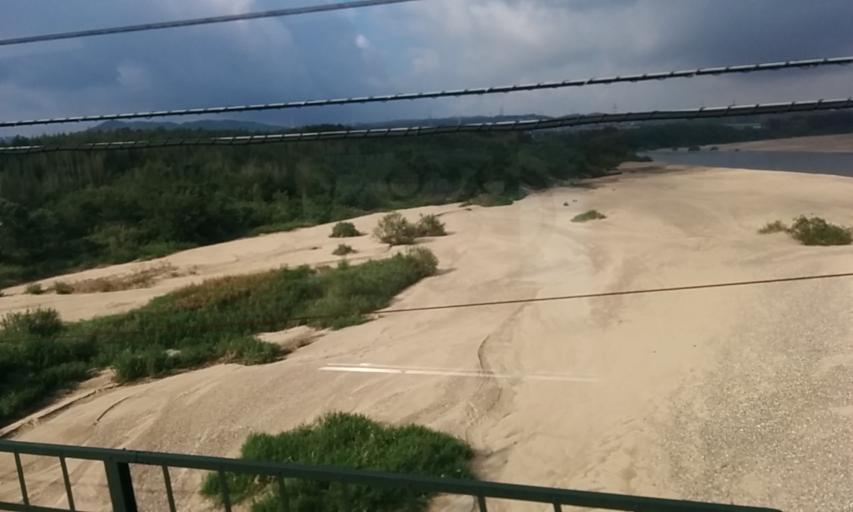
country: JP
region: Kyoto
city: Tanabe
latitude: 34.8336
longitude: 135.7737
